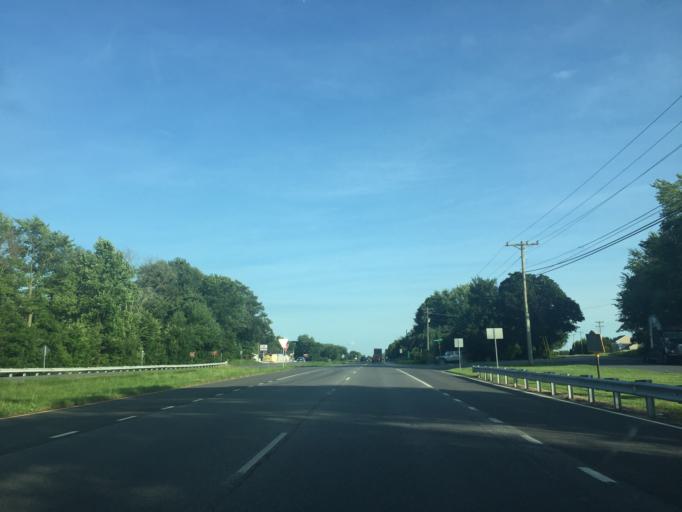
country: US
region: Delaware
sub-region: Kent County
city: Cheswold
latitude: 39.2429
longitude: -75.5875
